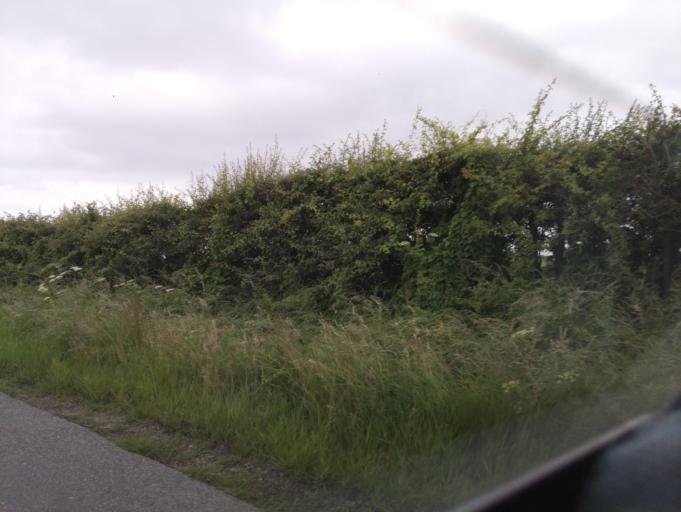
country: GB
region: England
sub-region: District of Rutland
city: Langham
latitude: 52.6701
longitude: -0.7612
